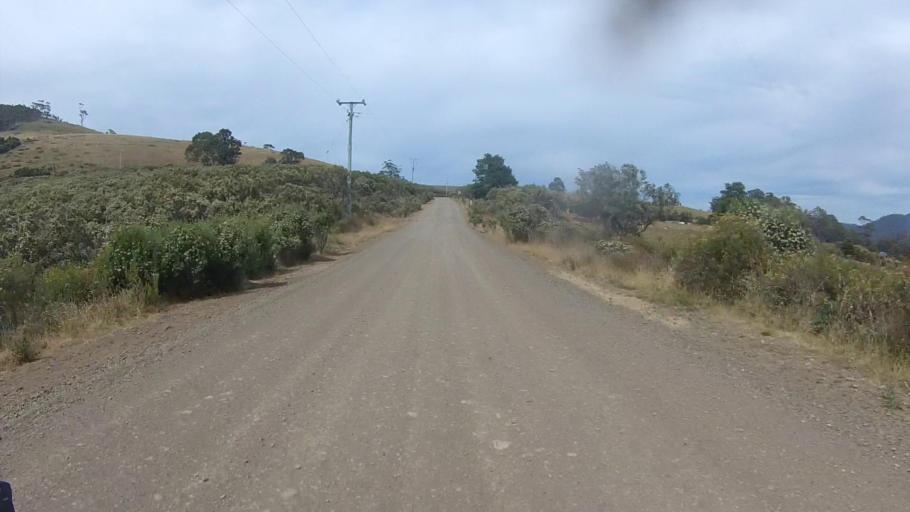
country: AU
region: Tasmania
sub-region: Sorell
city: Sorell
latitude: -42.7751
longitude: 147.8289
